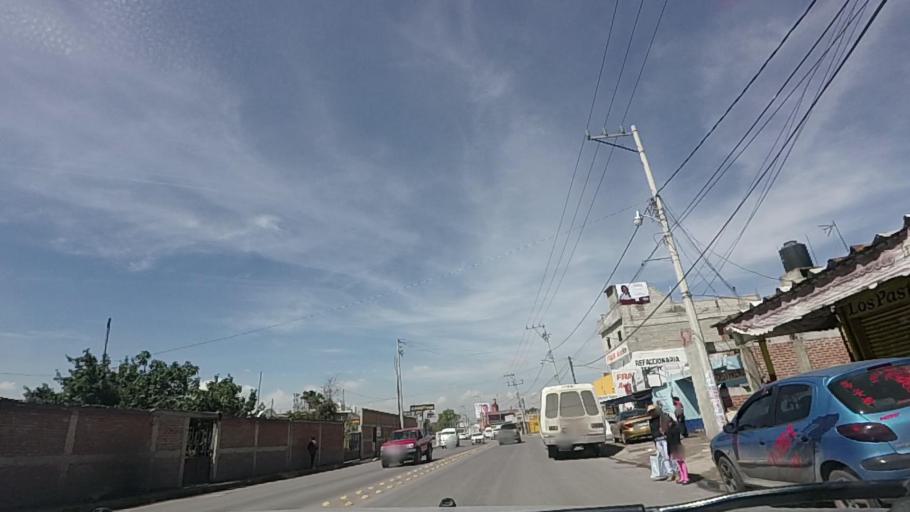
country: MX
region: Mexico
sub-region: Cuautitlan
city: Barrio Tlatenco
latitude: 19.7364
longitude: -99.1828
